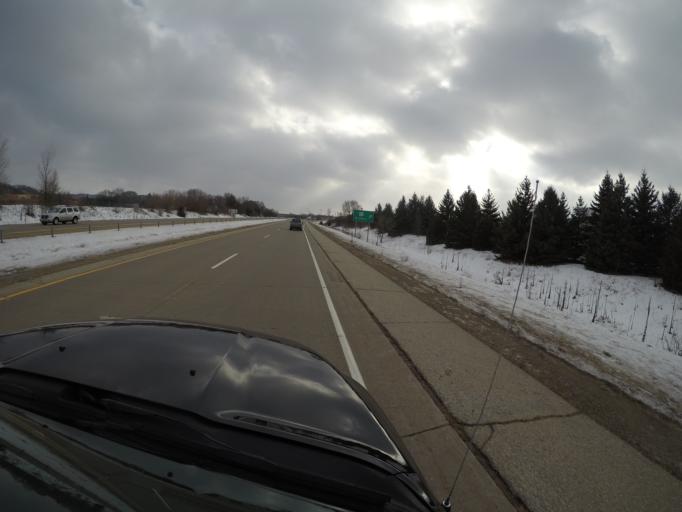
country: US
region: Wisconsin
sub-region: La Crosse County
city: Holmen
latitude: 43.9288
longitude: -91.2431
